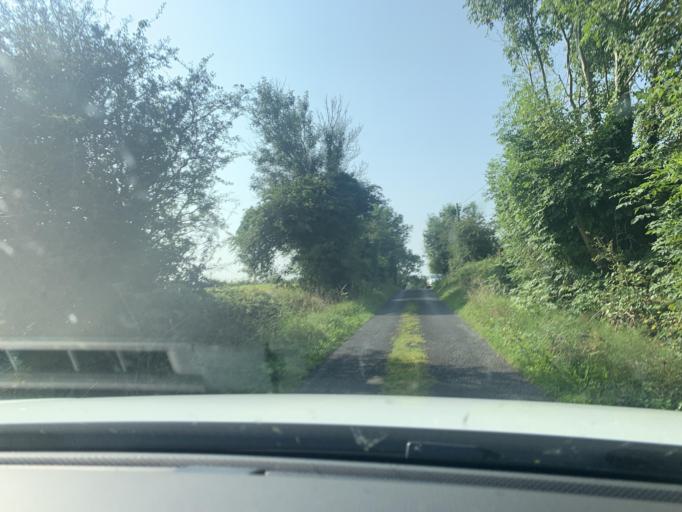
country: IE
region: Connaught
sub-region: Maigh Eo
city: Ballyhaunis
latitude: 53.8032
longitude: -8.7442
